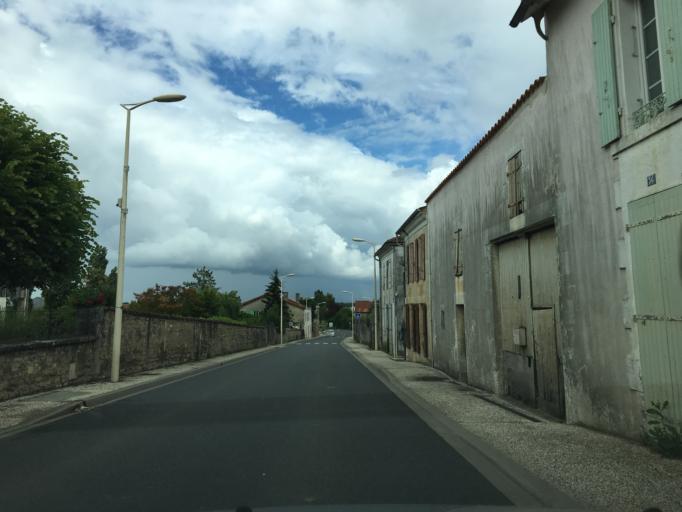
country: FR
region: Poitou-Charentes
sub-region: Departement de la Charente-Maritime
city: Saint-Jean-d'Angely
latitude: 46.0482
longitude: -0.5118
